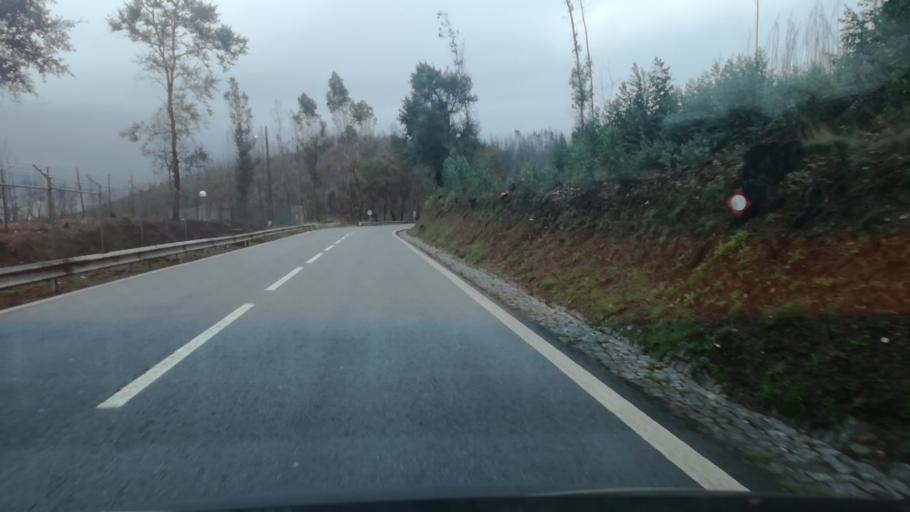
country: PT
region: Braga
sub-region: Braga
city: Braga
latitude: 41.5268
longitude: -8.3893
